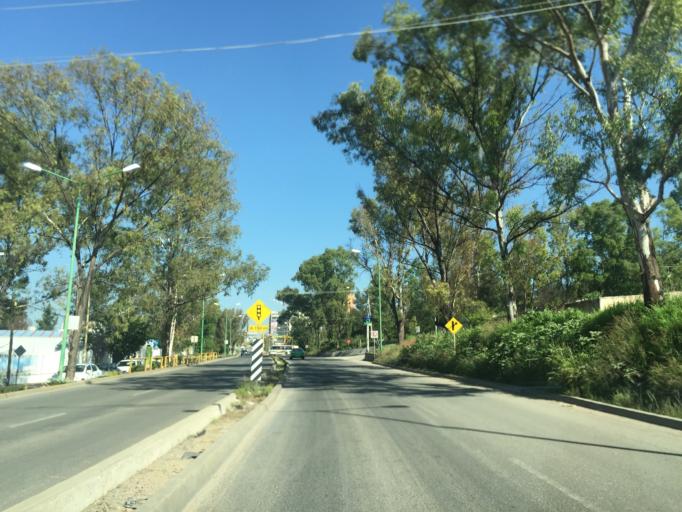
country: MX
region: Guanajuato
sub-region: Leon
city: La Ermita
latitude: 21.1674
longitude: -101.7293
